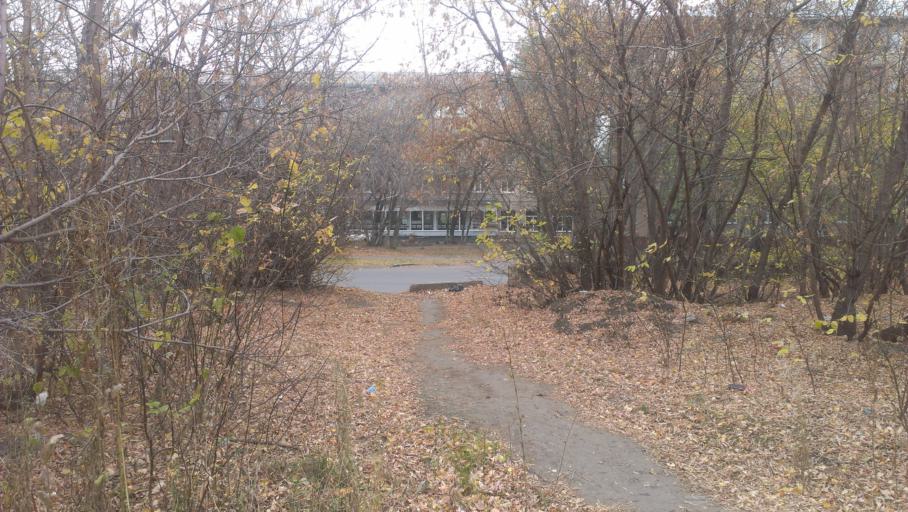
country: RU
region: Altai Krai
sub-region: Gorod Barnaulskiy
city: Barnaul
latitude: 53.3624
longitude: 83.6916
